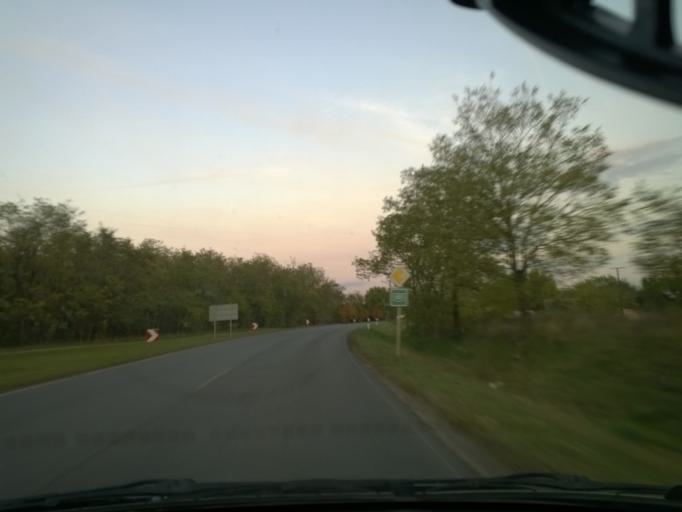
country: HU
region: Csongrad
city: Csongrad
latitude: 46.7208
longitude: 20.0954
